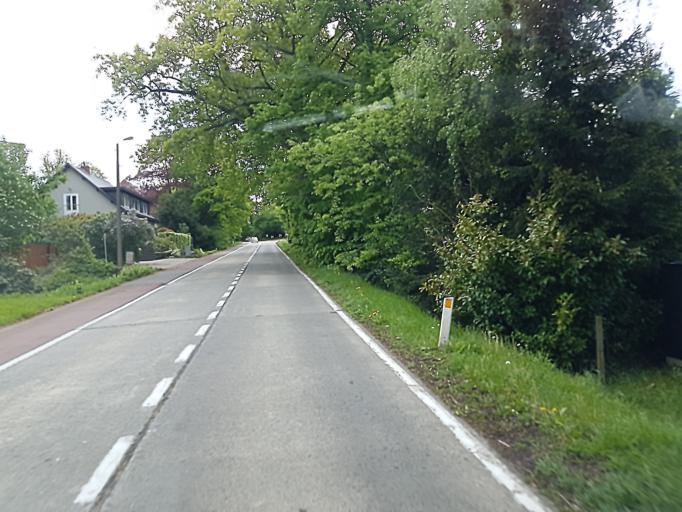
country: BE
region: Flanders
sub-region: Provincie Vlaams-Brabant
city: Diest
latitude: 51.0001
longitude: 5.0307
